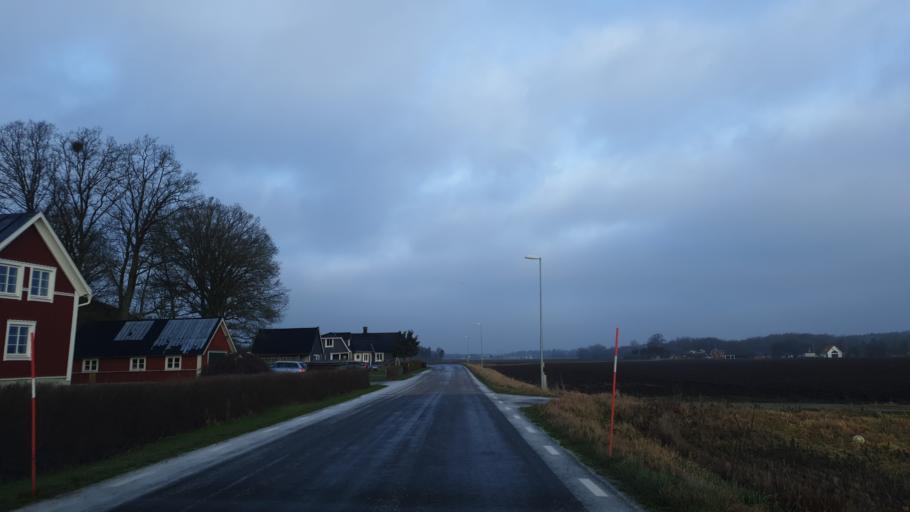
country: SE
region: Blekinge
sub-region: Karlshamns Kommun
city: Morrum
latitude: 56.1660
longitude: 14.7479
